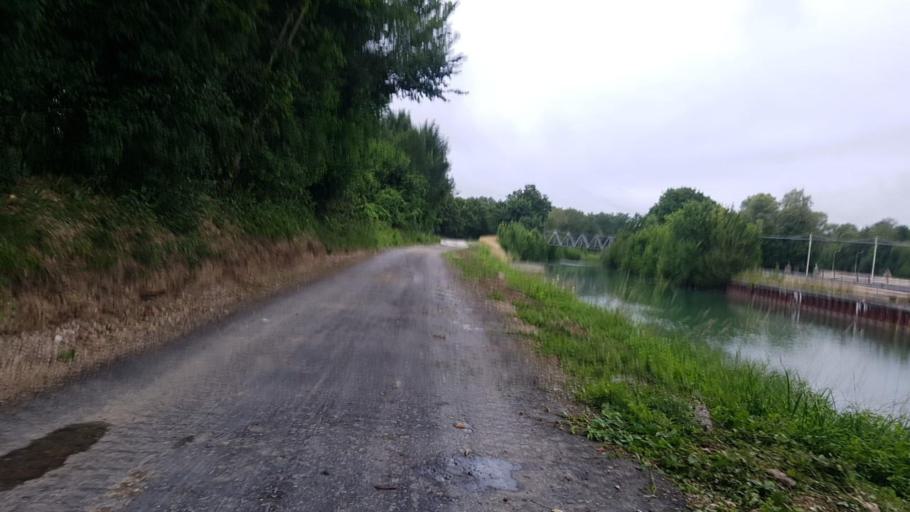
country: FR
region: Champagne-Ardenne
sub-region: Departement de la Marne
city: Sarry
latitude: 48.8463
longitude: 4.4912
